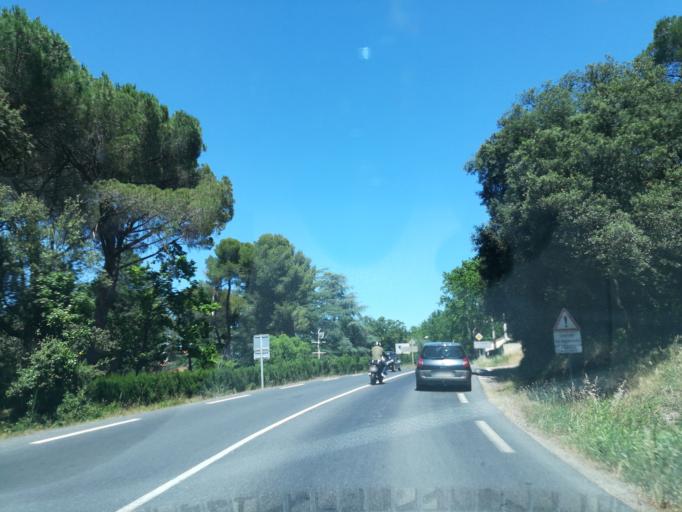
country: FR
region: Languedoc-Roussillon
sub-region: Departement des Pyrenees-Orientales
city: el Volo
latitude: 42.5084
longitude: 2.8254
